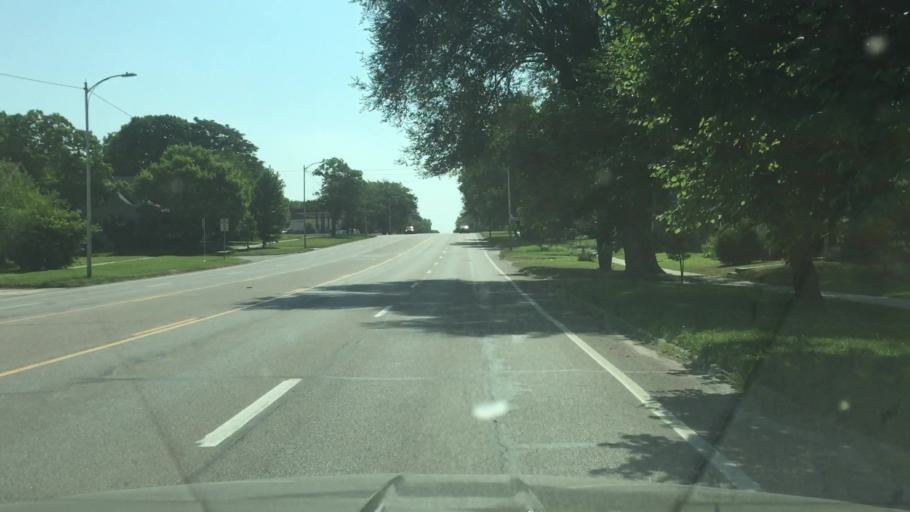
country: US
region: Missouri
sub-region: Pettis County
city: Sedalia
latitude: 38.7035
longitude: -93.2107
